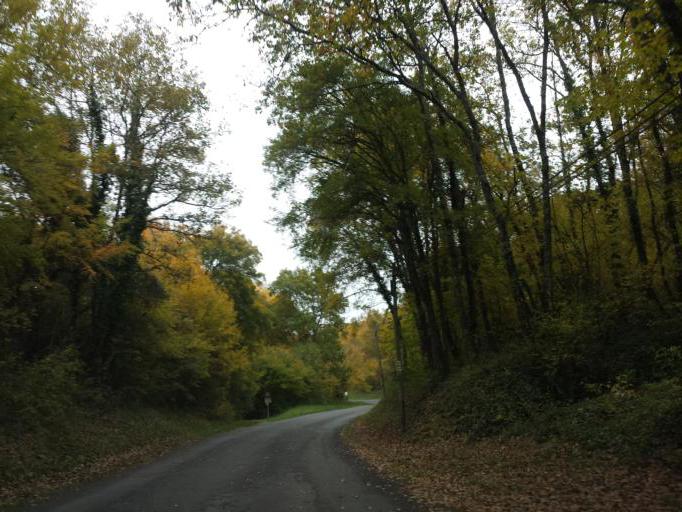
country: FR
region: Poitou-Charentes
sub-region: Departement de la Charente
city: Puymoyen
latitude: 45.6084
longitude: 0.1801
